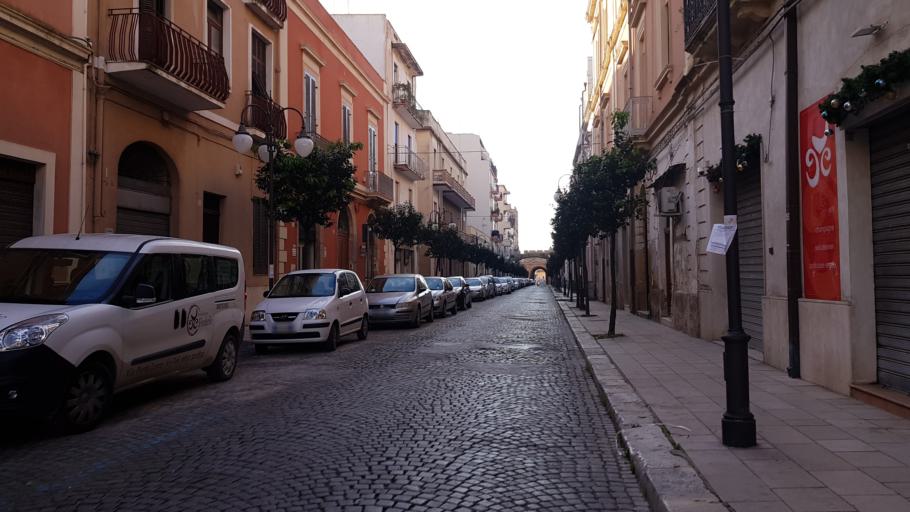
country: IT
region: Apulia
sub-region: Provincia di Brindisi
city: Brindisi
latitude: 40.6350
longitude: 17.9450
